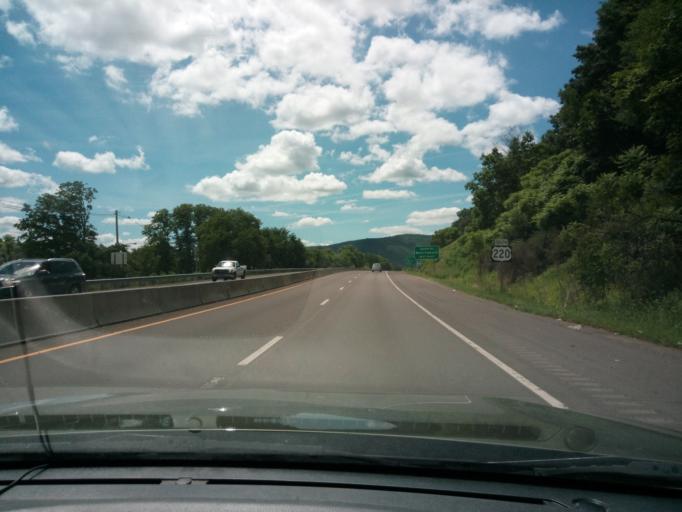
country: US
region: Pennsylvania
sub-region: Bradford County
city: South Waverly
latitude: 41.9972
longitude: -76.5486
